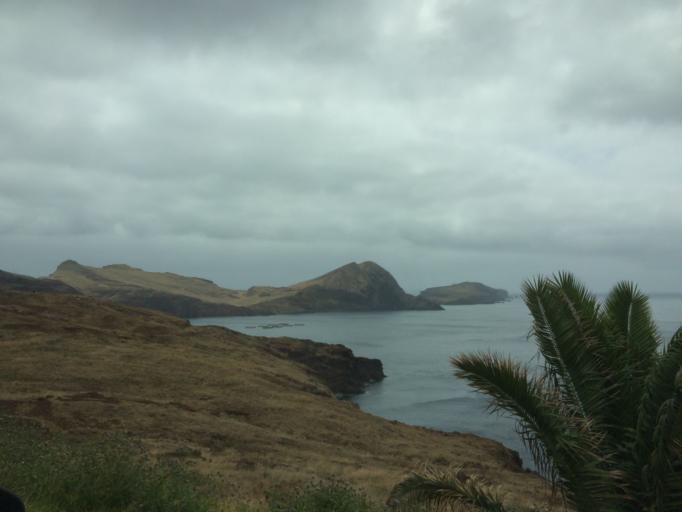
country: PT
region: Madeira
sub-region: Machico
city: Canical
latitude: 32.7415
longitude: -16.7028
